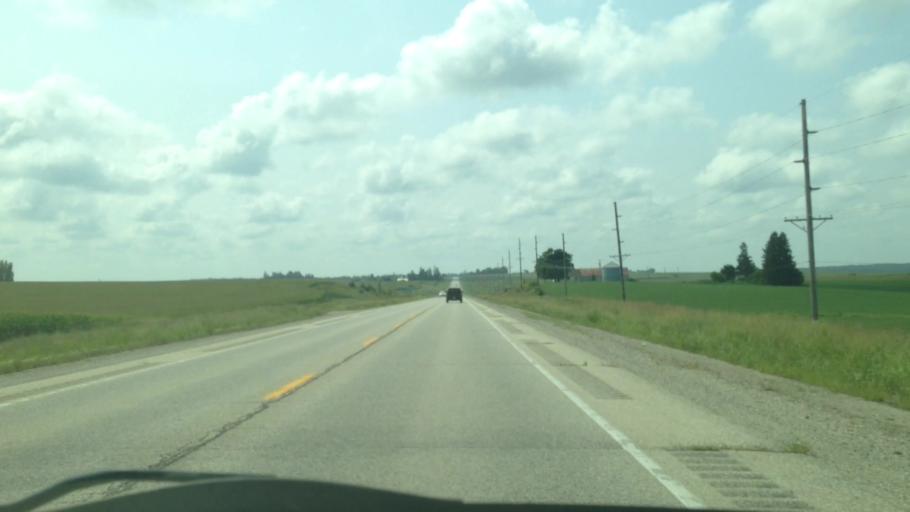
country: US
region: Iowa
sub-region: Benton County
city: Walford
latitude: 41.8661
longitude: -91.8702
